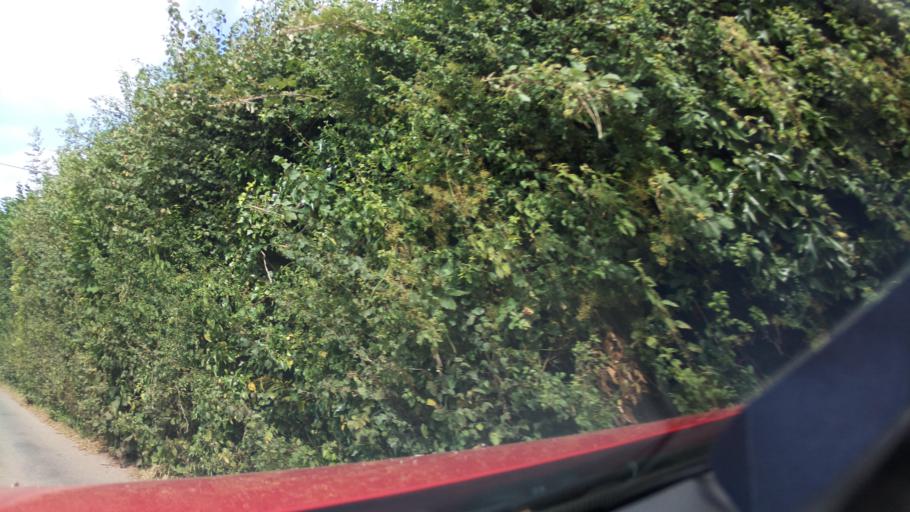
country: GB
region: England
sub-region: Devon
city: Marldon
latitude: 50.4166
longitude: -3.6250
